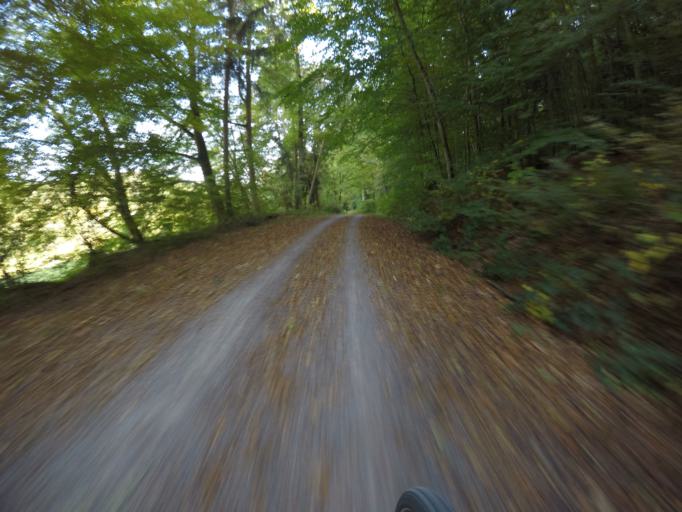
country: DE
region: Baden-Wuerttemberg
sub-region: Regierungsbezirk Stuttgart
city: Filderstadt
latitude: 48.6312
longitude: 9.1875
